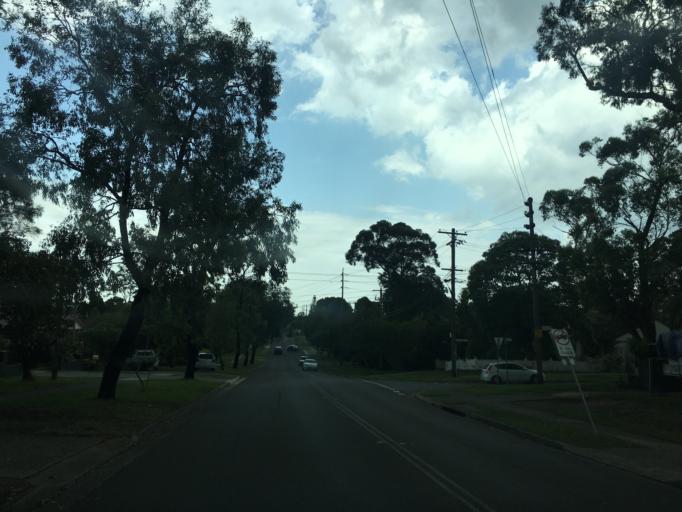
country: AU
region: New South Wales
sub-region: Ryde
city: Marsfield
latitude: -33.7901
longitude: 151.1047
